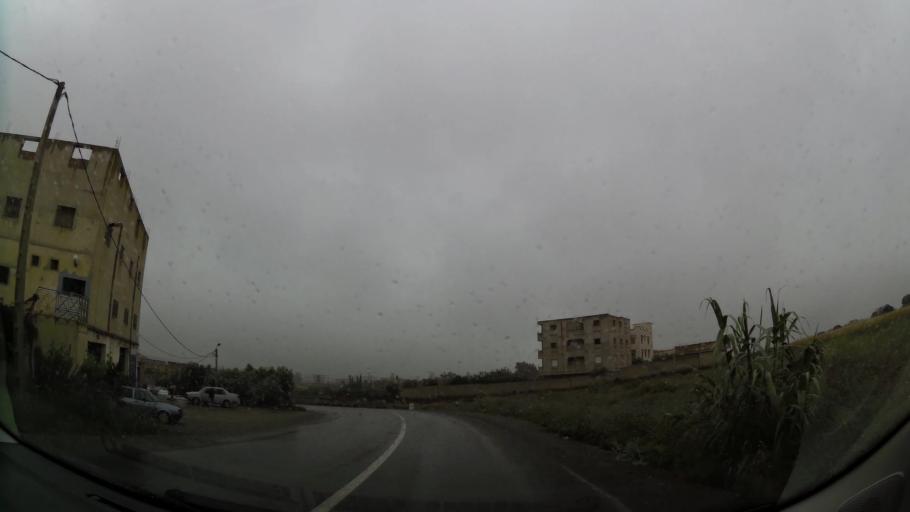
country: MA
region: Oriental
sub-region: Nador
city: Boudinar
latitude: 35.1416
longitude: -3.6148
